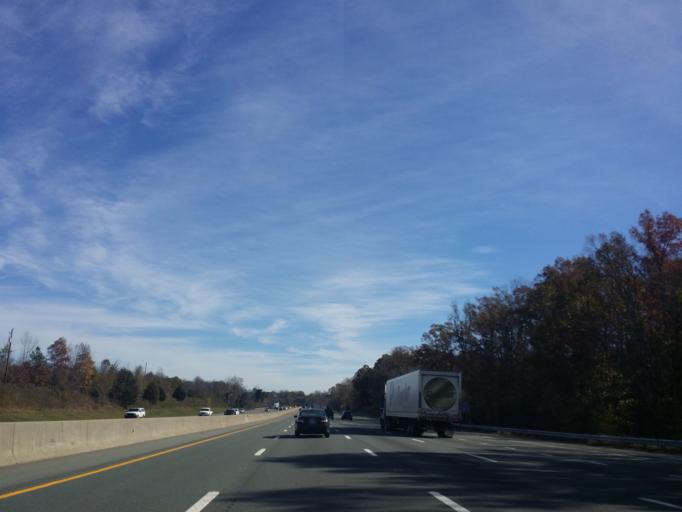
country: US
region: North Carolina
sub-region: Alamance County
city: Mebane
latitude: 36.0683
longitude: -79.2922
